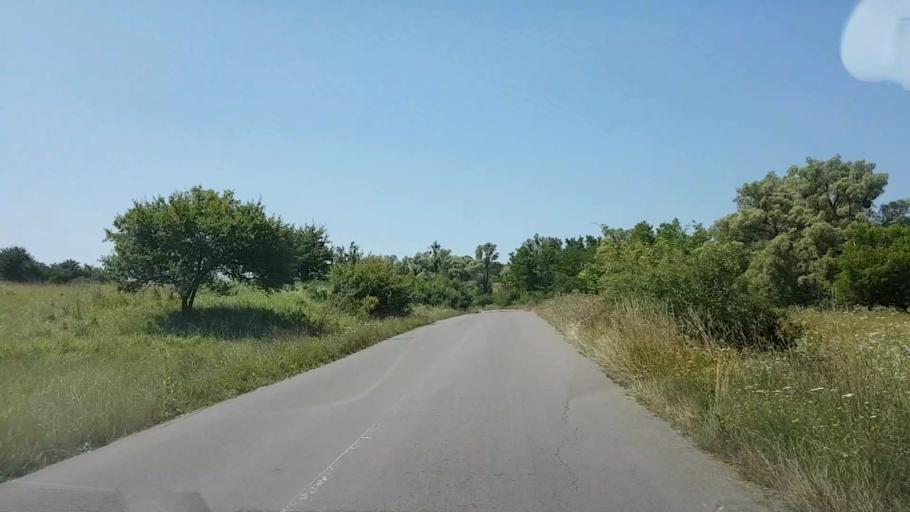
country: RO
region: Brasov
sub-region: Comuna Cincu
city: Cincu
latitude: 45.9503
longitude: 24.7839
